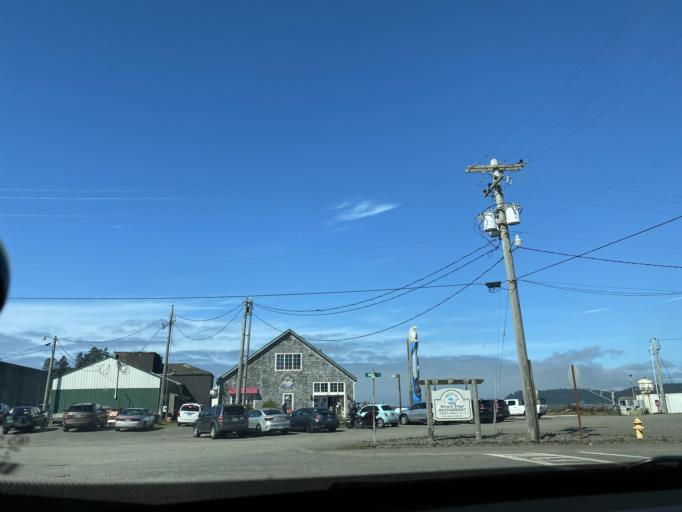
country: US
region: Washington
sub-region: Clallam County
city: Forks
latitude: 47.9093
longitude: -124.6372
